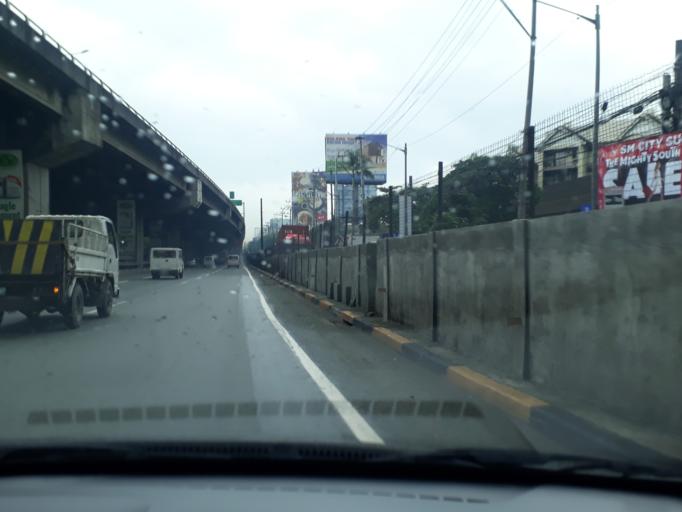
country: PH
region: Metro Manila
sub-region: Makati City
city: Makati City
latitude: 14.5065
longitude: 121.0350
